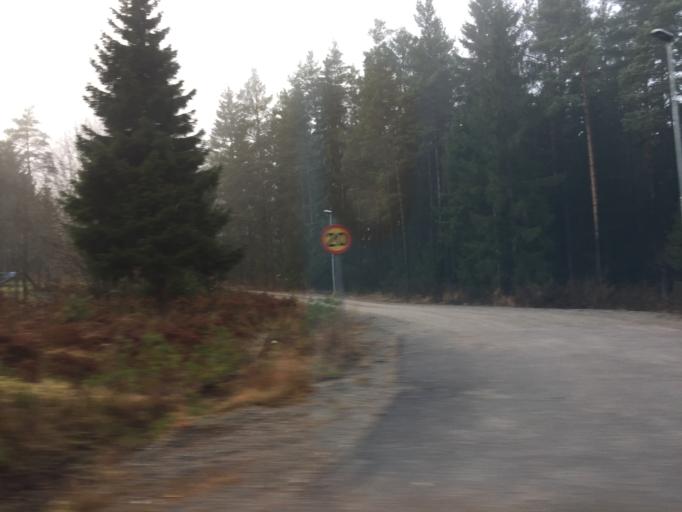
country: SE
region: Stockholm
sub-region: Nynashamns Kommun
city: Osmo
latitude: 59.0642
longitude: 17.8748
